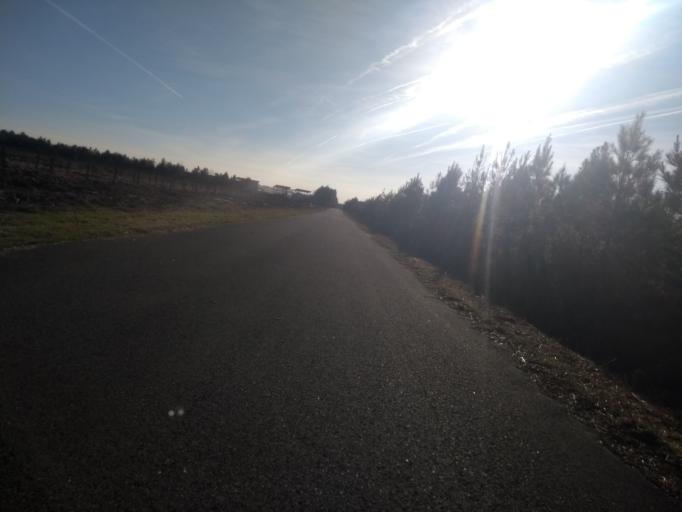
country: FR
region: Aquitaine
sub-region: Departement de la Gironde
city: Le Barp
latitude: 44.6184
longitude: -0.7916
